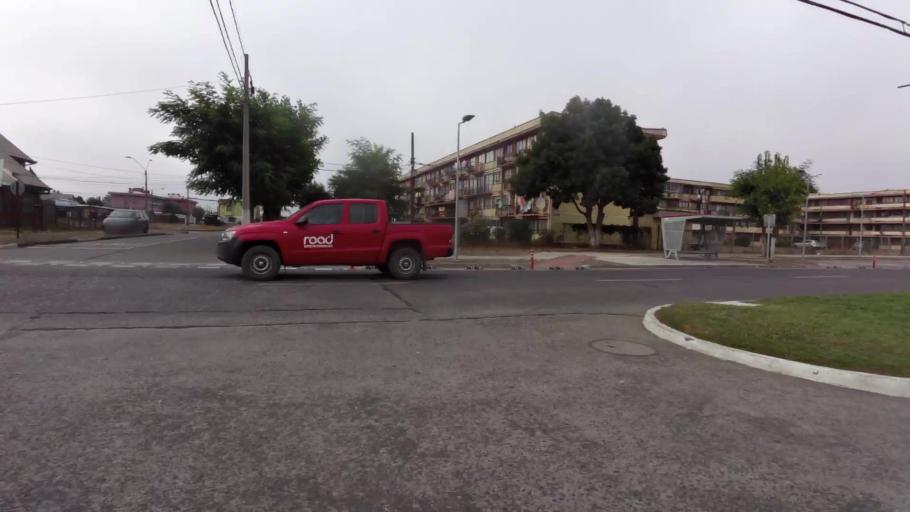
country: CL
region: Biobio
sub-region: Provincia de Concepcion
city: Concepcion
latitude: -36.7900
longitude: -73.0892
